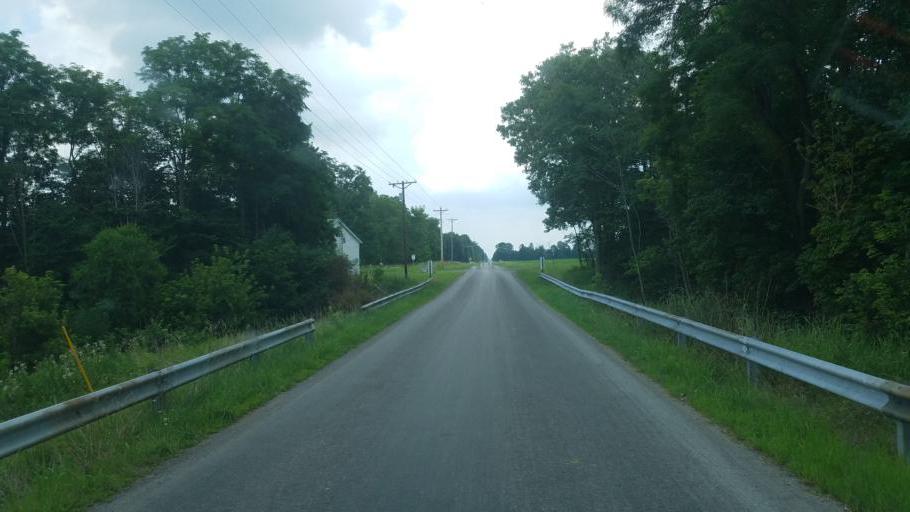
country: US
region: Ohio
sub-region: Hardin County
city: Kenton
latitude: 40.5787
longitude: -83.5757
